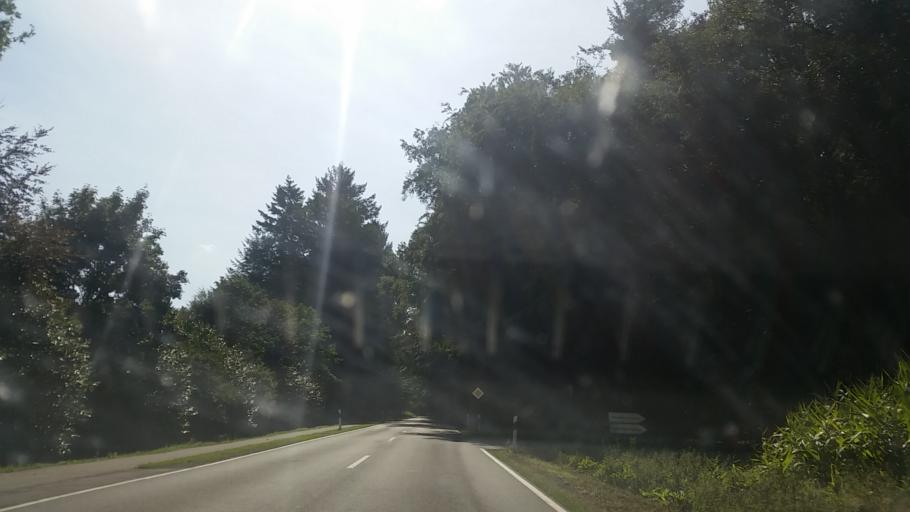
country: DE
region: Lower Saxony
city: Ankum
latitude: 52.5227
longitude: 7.8987
